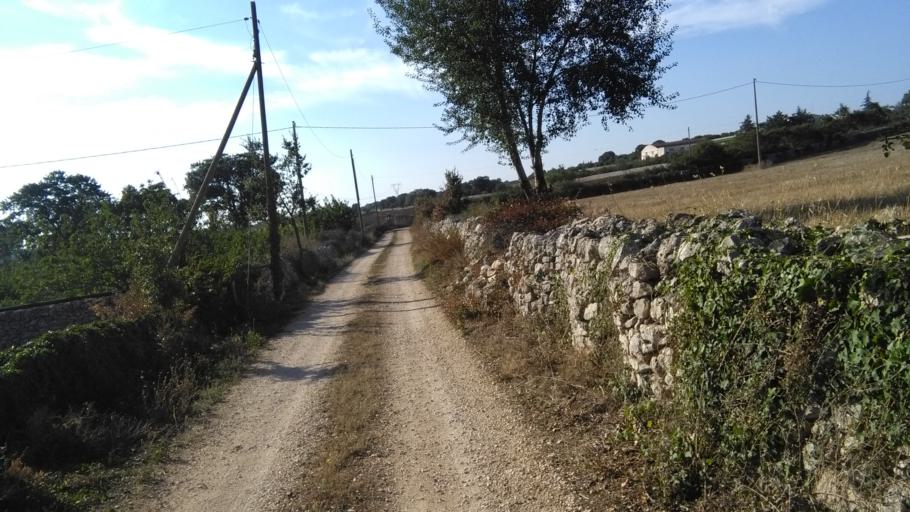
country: IT
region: Apulia
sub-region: Provincia di Bari
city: Putignano
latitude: 40.8215
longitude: 17.0569
